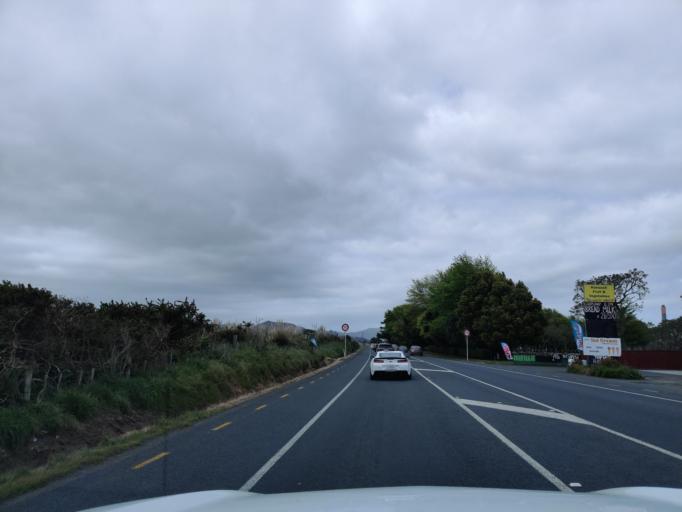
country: NZ
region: Waikato
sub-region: Waikato District
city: Te Kauwhata
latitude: -37.5293
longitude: 175.1592
